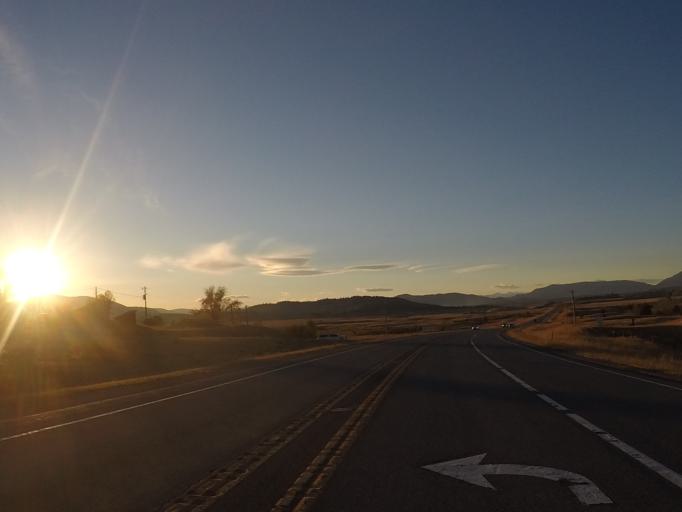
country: US
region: Montana
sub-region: Missoula County
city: Seeley Lake
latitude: 47.0206
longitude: -113.1226
